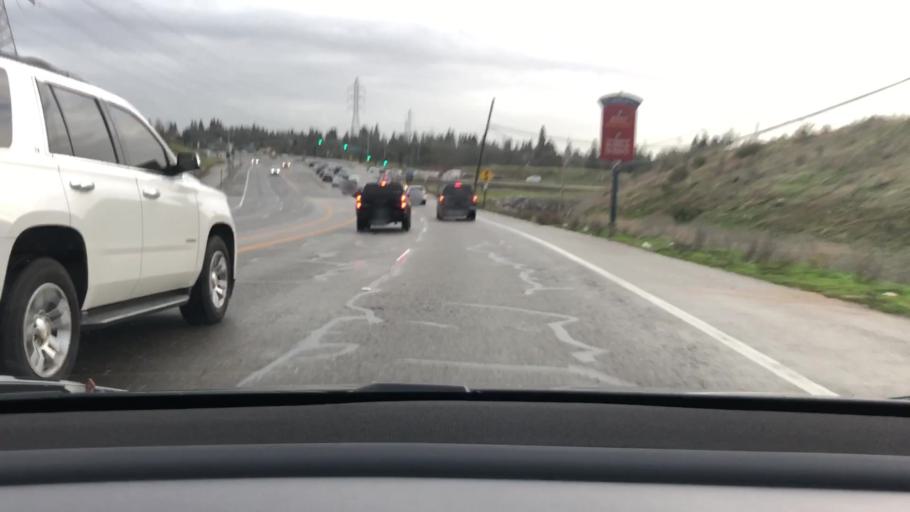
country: US
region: California
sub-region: Sacramento County
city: Folsom
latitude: 38.6954
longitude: -121.1440
